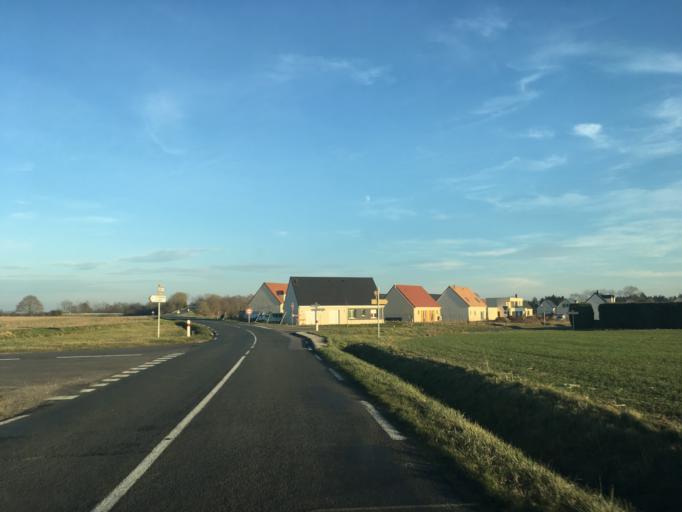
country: FR
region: Haute-Normandie
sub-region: Departement de l'Eure
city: La Chapelle-Reanville
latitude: 49.0657
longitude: 1.4091
